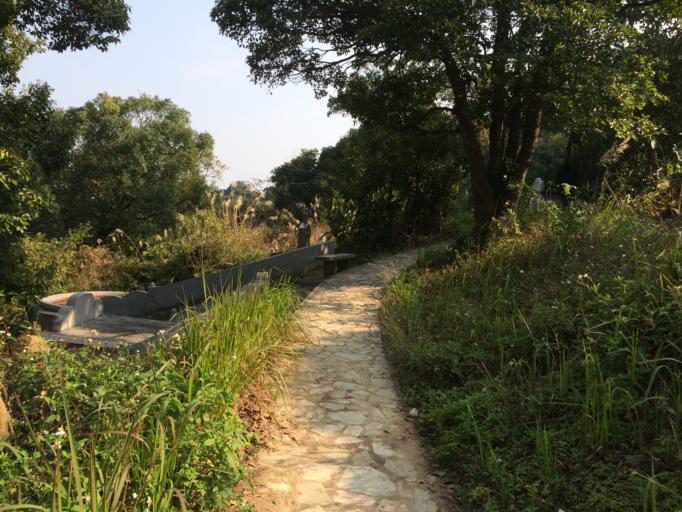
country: HK
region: Tai Po
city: Tai Po
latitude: 22.4526
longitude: 114.2141
